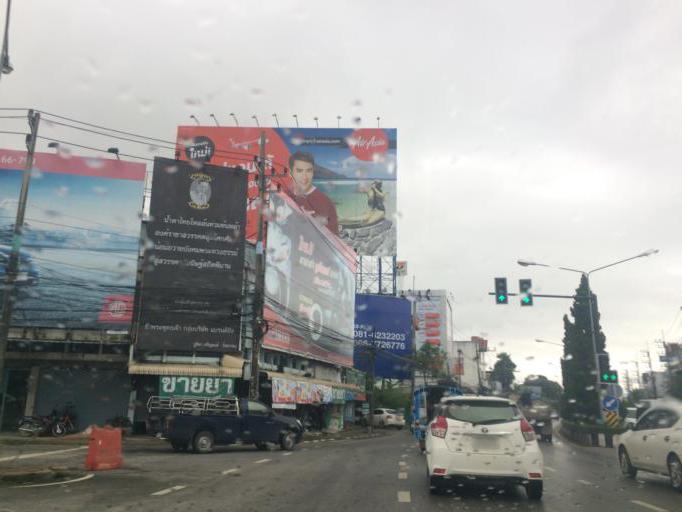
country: TH
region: Chiang Rai
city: Chiang Rai
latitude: 19.9105
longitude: 99.8404
